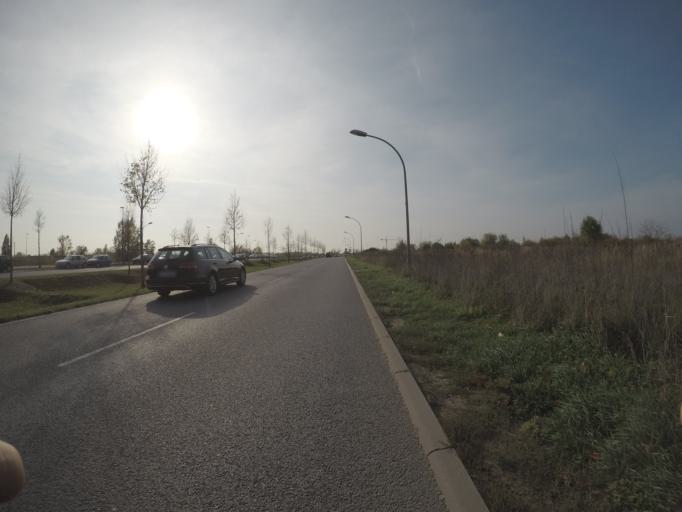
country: DE
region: Brandenburg
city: Schonefeld
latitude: 52.3943
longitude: 13.5122
